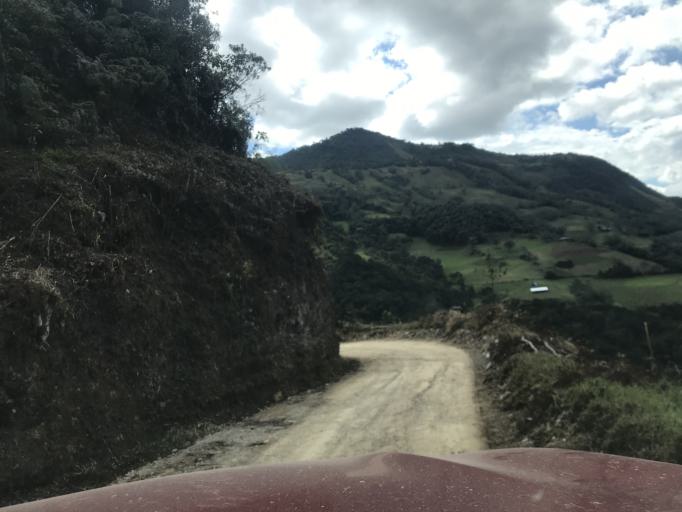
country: PE
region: Cajamarca
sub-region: Provincia de Chota
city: Querocoto
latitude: -6.3491
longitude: -79.0575
